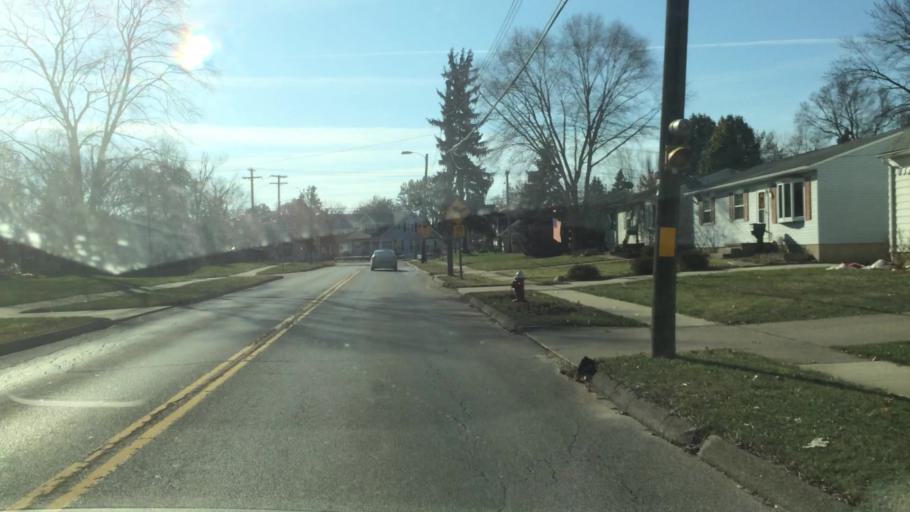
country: US
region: Ohio
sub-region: Summit County
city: Cuyahoga Falls
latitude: 41.1367
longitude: -81.4689
